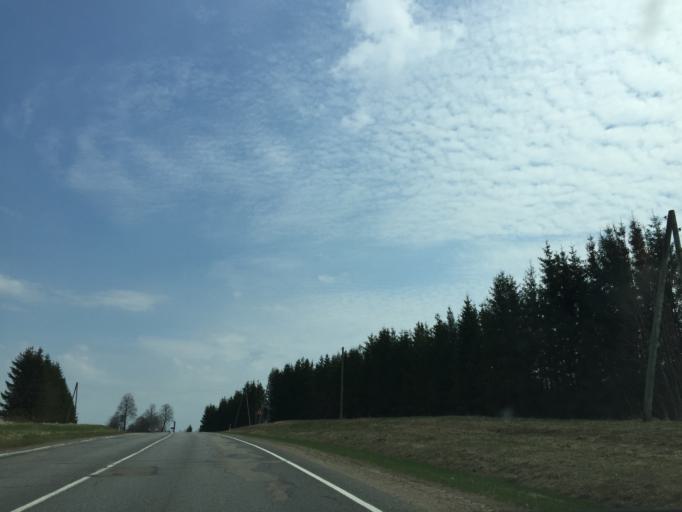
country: LV
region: Apes Novads
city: Ape
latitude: 57.4541
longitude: 26.3538
